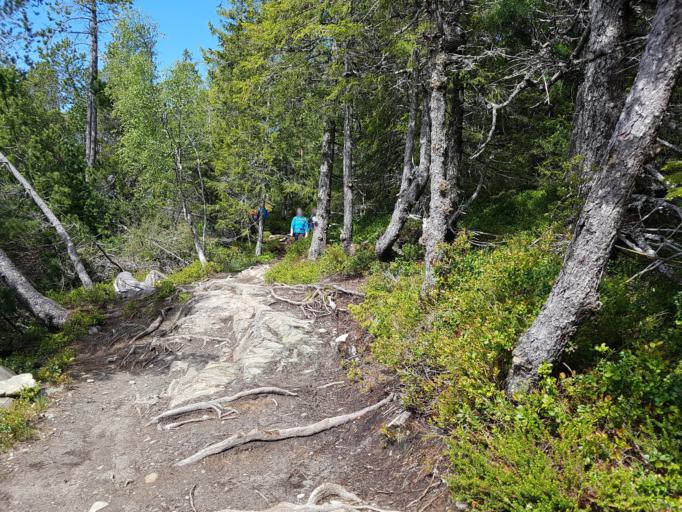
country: NO
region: Sor-Trondelag
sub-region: Trondheim
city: Trondheim
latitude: 63.4291
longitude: 10.3055
